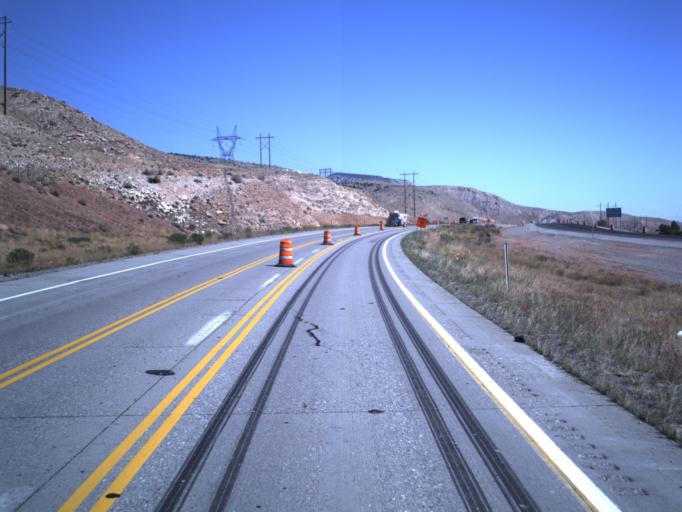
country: US
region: Utah
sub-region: Sevier County
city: Richfield
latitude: 38.7801
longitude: -112.0954
